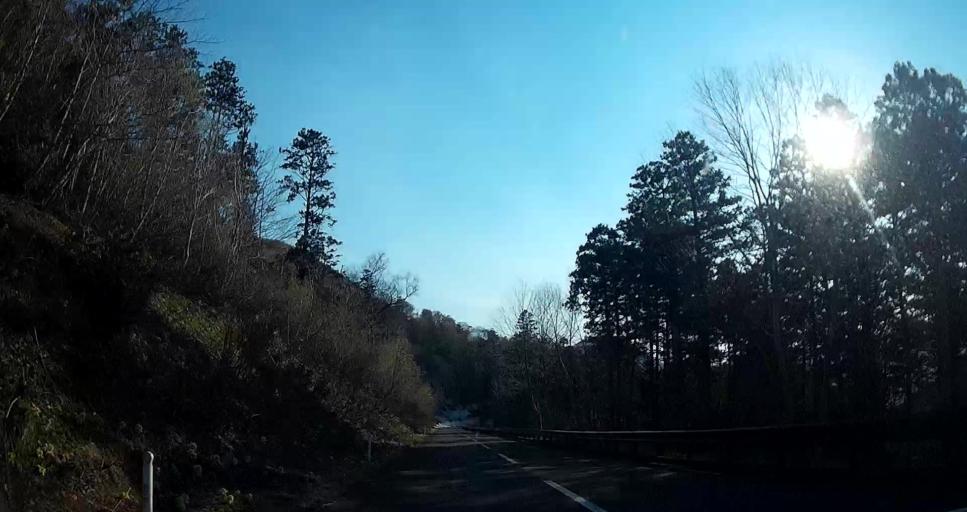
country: JP
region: Aomori
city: Mutsu
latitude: 41.3093
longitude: 141.1167
